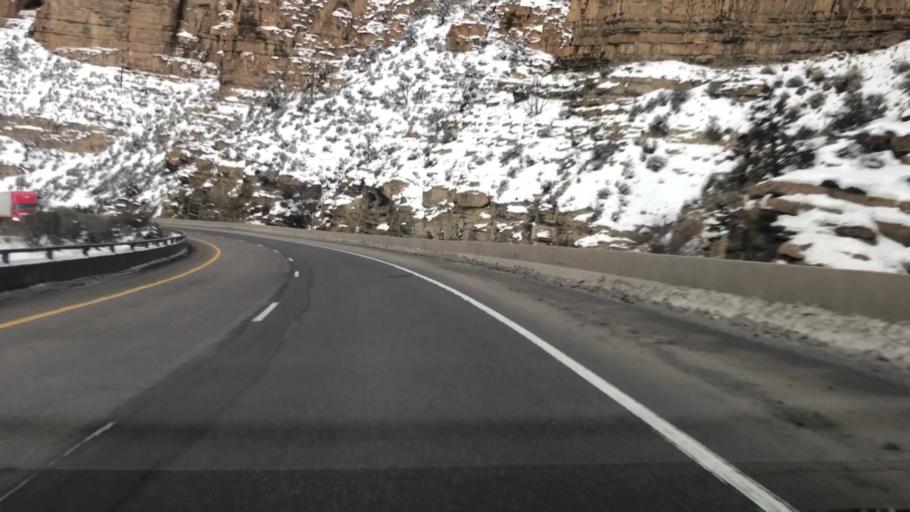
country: US
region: Colorado
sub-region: Eagle County
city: Gypsum
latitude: 39.6250
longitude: -107.1202
